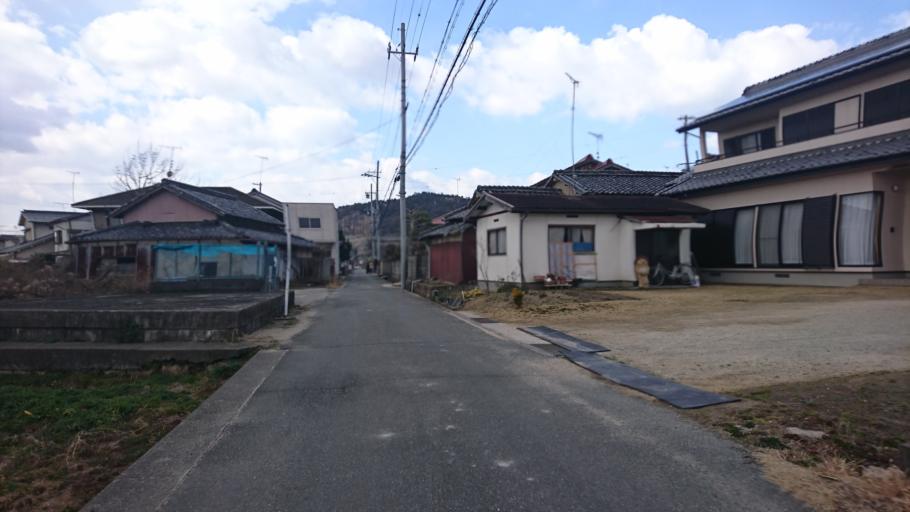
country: JP
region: Hyogo
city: Kakogawacho-honmachi
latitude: 34.7975
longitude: 134.8067
